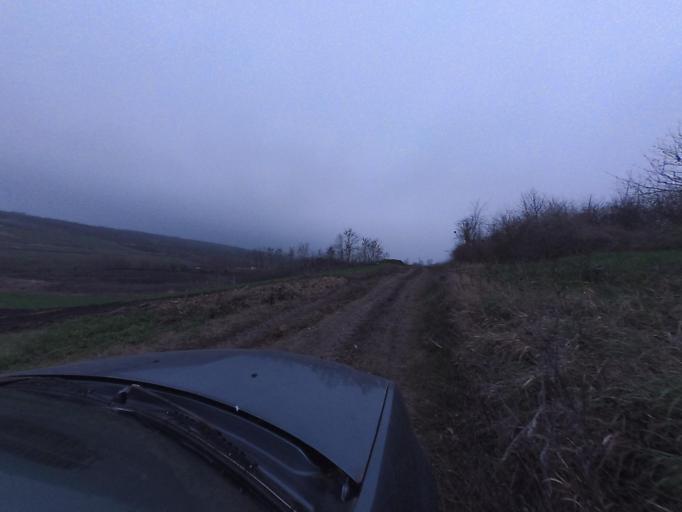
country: RO
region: Galati
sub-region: Comuna Balabanesti
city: Balabanesti
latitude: 46.1344
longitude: 27.7501
